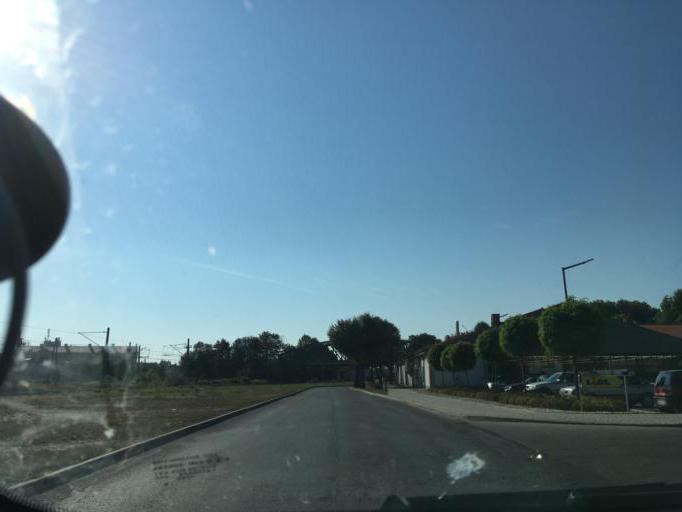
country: PL
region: Subcarpathian Voivodeship
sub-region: Przemysl
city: Przemysl
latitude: 49.7827
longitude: 22.7916
